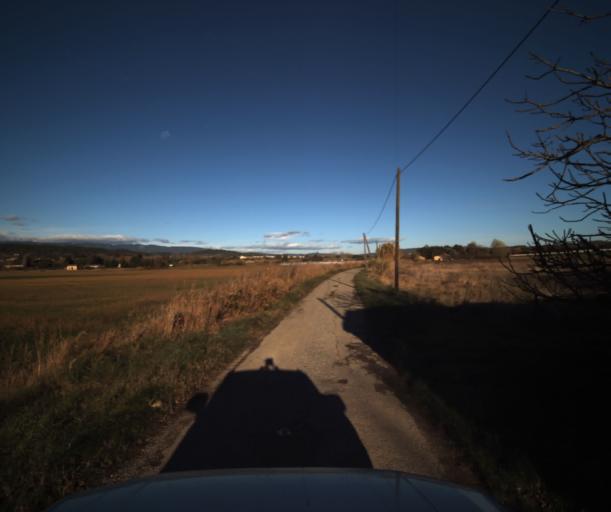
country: FR
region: Provence-Alpes-Cote d'Azur
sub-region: Departement du Vaucluse
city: Pertuis
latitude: 43.6843
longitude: 5.4775
